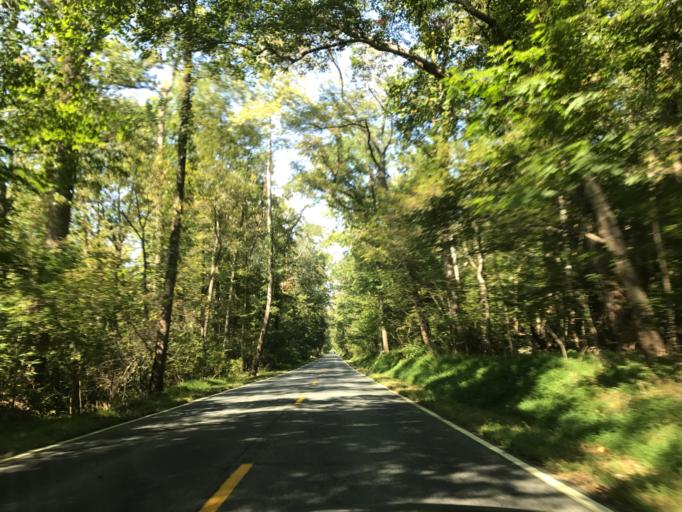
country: US
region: Maryland
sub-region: Cecil County
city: Rising Sun
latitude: 39.6463
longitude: -76.1515
